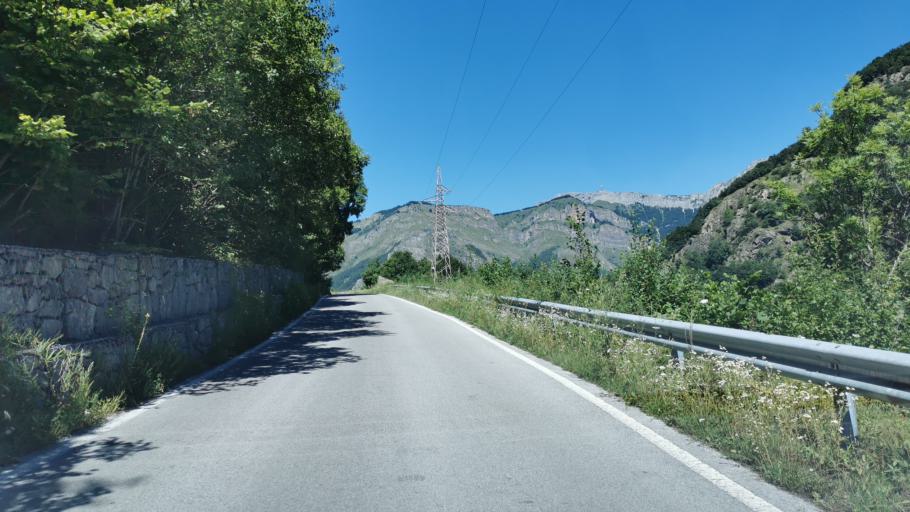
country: IT
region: Piedmont
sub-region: Provincia di Cuneo
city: Entracque
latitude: 44.2190
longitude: 7.3860
